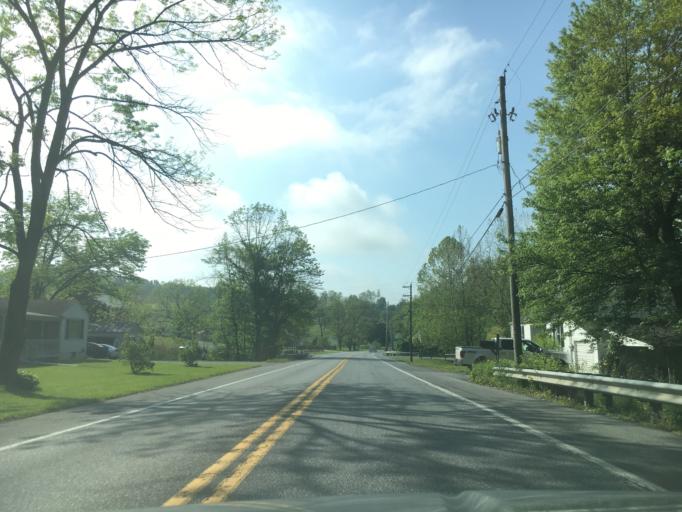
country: US
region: Pennsylvania
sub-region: Berks County
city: New Berlinville
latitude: 40.3553
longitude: -75.6644
